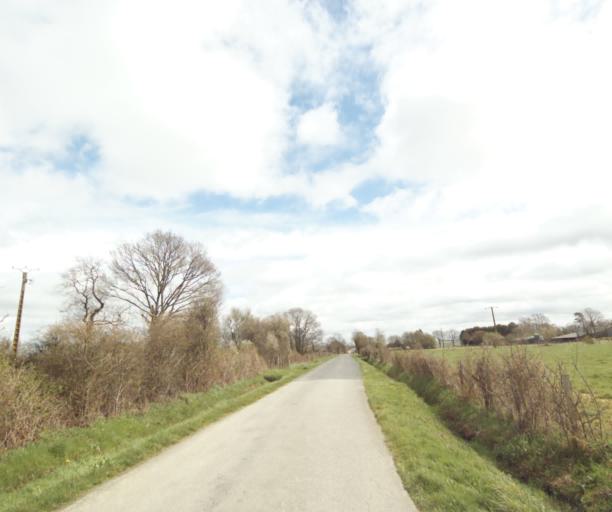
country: FR
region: Pays de la Loire
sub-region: Departement de la Loire-Atlantique
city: Bouvron
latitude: 47.4354
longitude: -1.8546
